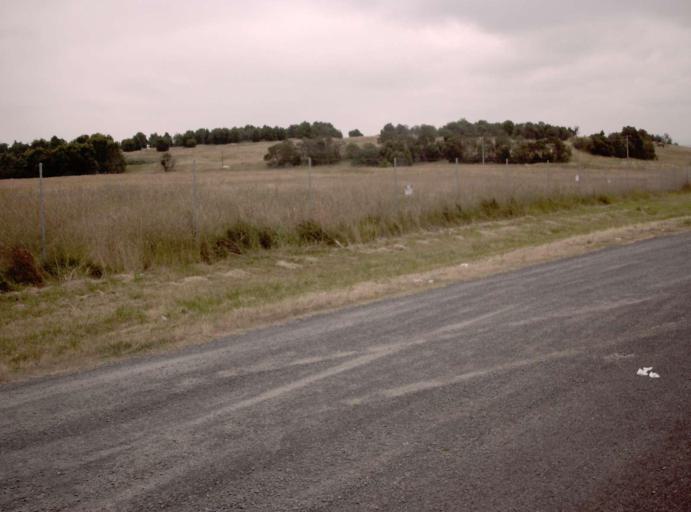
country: AU
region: Victoria
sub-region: Latrobe
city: Morwell
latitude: -38.2363
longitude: 146.3688
